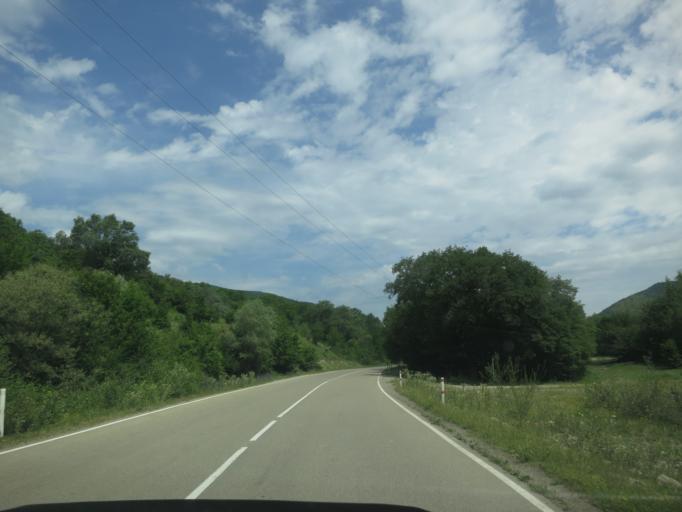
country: GE
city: Didi Lilo
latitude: 41.8255
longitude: 45.1376
